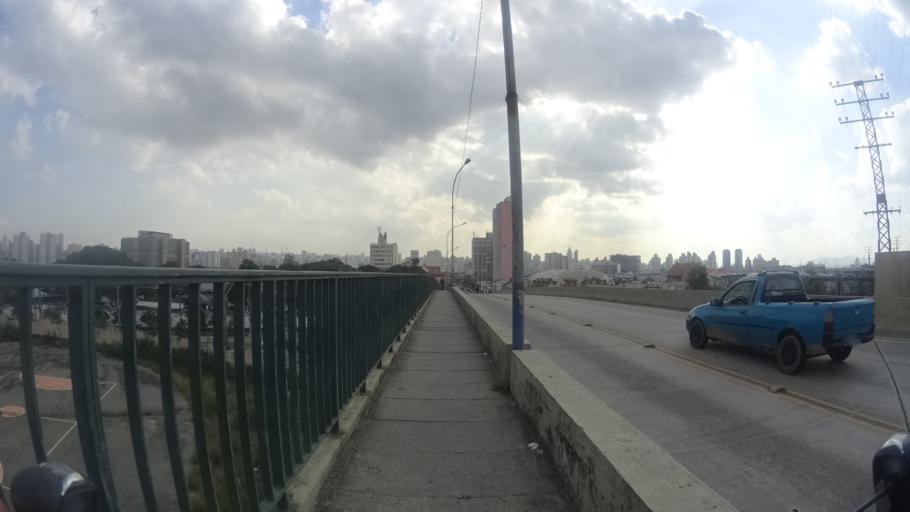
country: BR
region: Sao Paulo
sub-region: Sao Paulo
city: Sao Paulo
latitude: -23.5547
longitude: -46.6103
